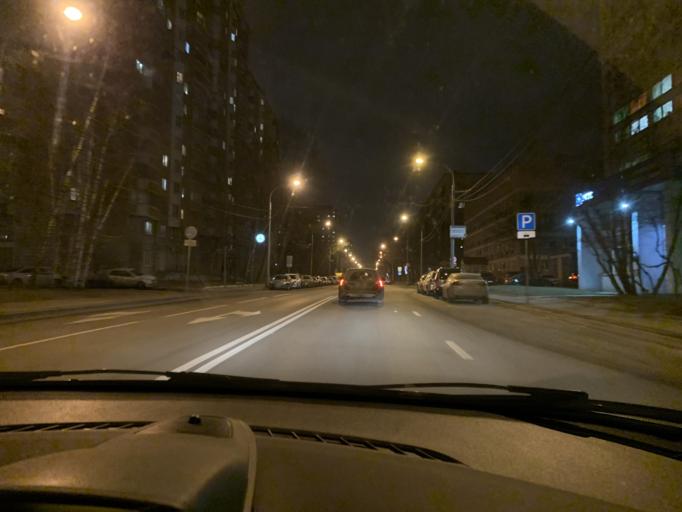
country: RU
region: Moscow
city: Likhobory
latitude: 55.8640
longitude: 37.5664
